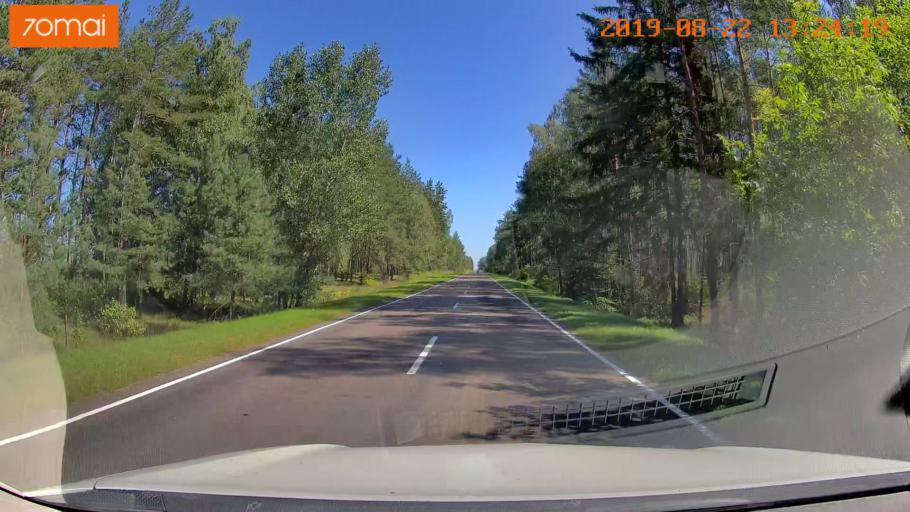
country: BY
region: Minsk
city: Urechcha
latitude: 53.2109
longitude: 28.0183
